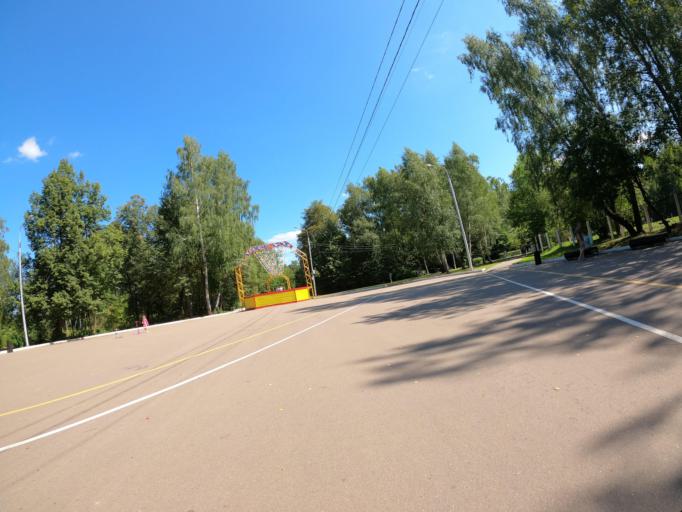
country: RU
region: Moskovskaya
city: Stupino
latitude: 54.8829
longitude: 38.0888
